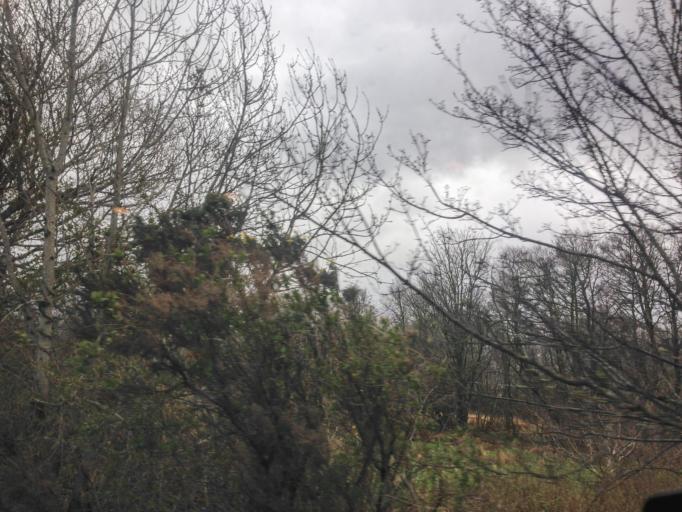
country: GB
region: Scotland
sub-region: Highland
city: Fort William
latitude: 56.8429
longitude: -5.1175
